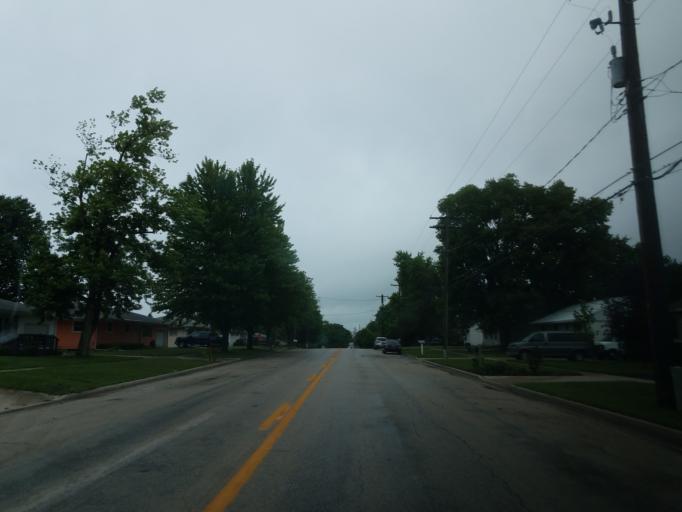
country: US
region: Illinois
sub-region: McLean County
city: Bloomington
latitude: 40.4643
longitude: -88.9818
